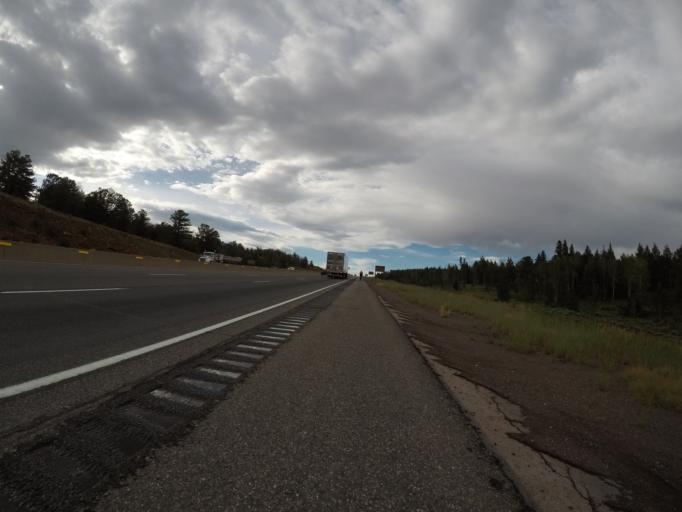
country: US
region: Wyoming
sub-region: Albany County
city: Laramie
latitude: 41.2521
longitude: -105.4456
